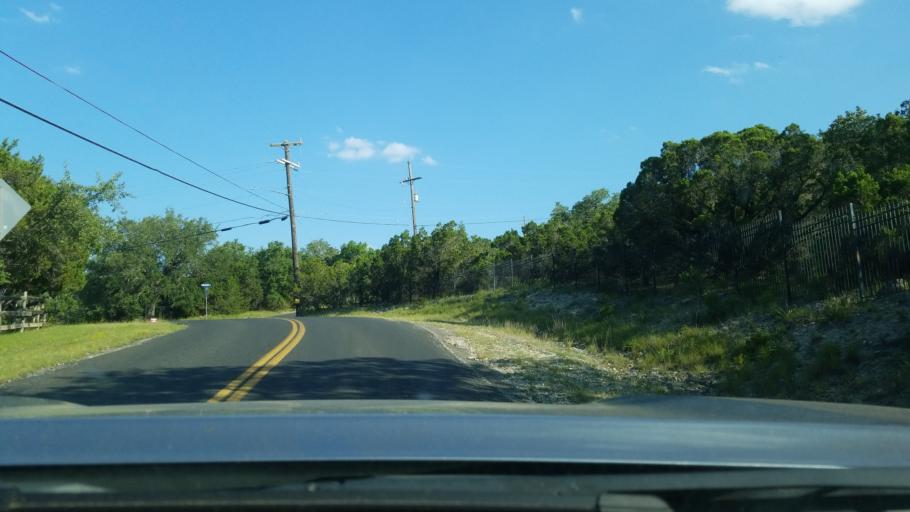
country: US
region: Texas
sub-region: Comal County
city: Bulverde
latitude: 29.7114
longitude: -98.4455
